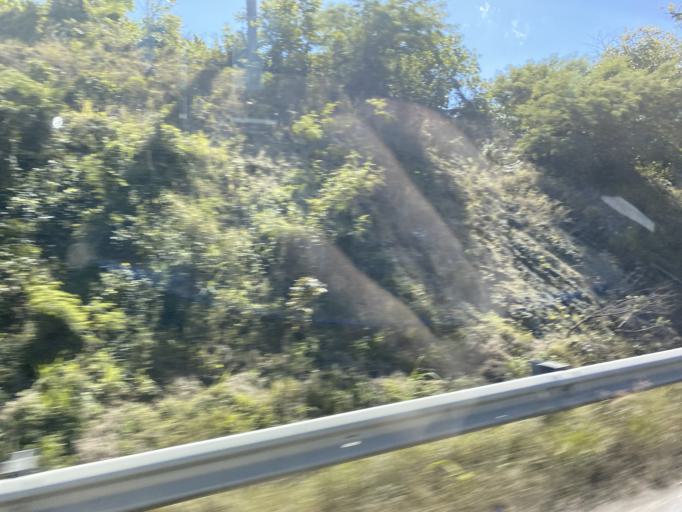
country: DO
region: Puerto Plata
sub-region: Puerto Plata
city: Puerto Plata
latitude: 19.8300
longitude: -70.7689
